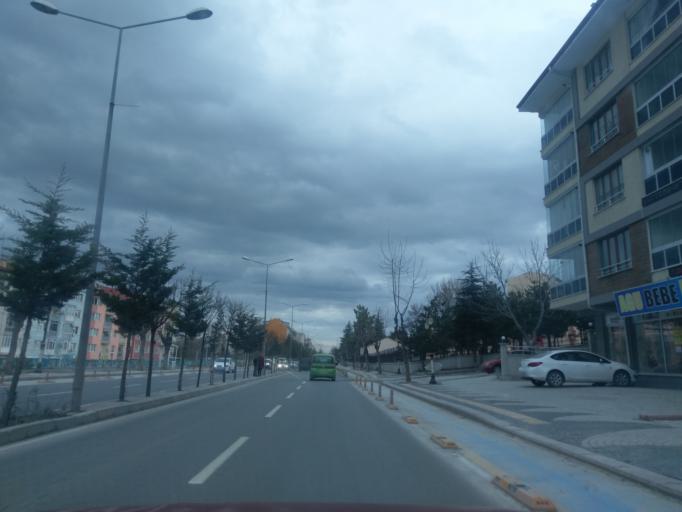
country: TR
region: Kuetahya
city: Kutahya
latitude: 39.4108
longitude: 30.0026
